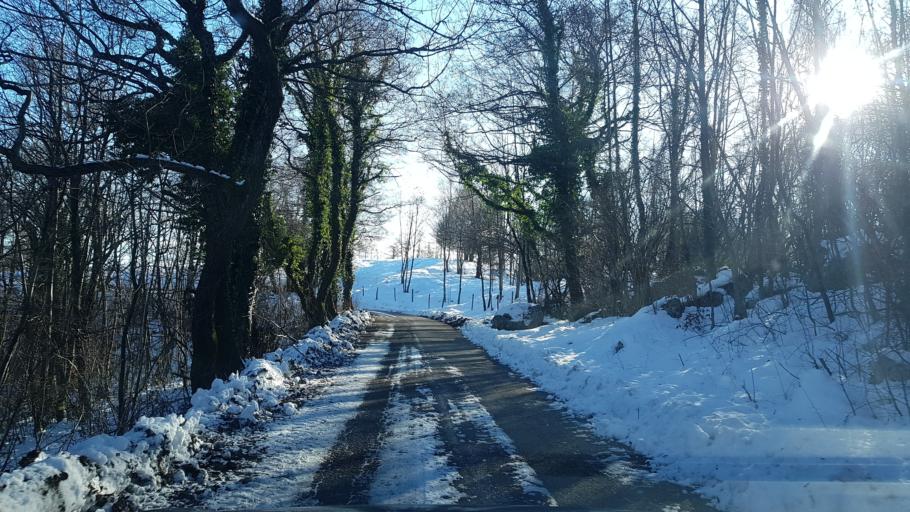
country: IT
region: Friuli Venezia Giulia
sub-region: Provincia di Udine
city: Forgaria nel Friuli
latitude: 46.2536
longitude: 12.9938
